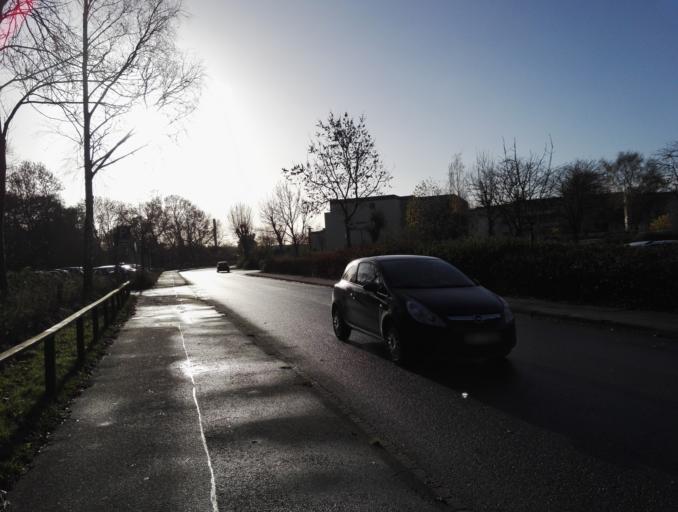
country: DE
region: Schleswig-Holstein
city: Wangels
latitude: 54.3090
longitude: 10.7979
